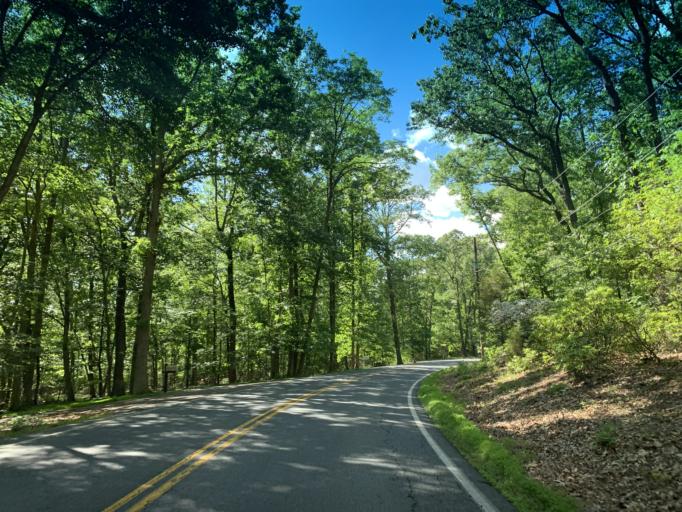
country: US
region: Maryland
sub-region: Cecil County
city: North East
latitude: 39.5595
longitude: -75.9326
